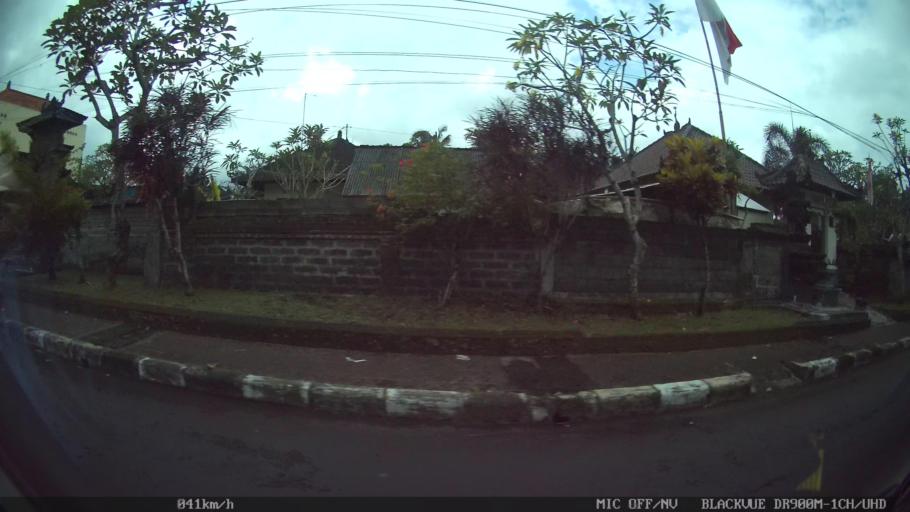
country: ID
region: Bali
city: Banjar Serangan
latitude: -8.5435
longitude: 115.1760
